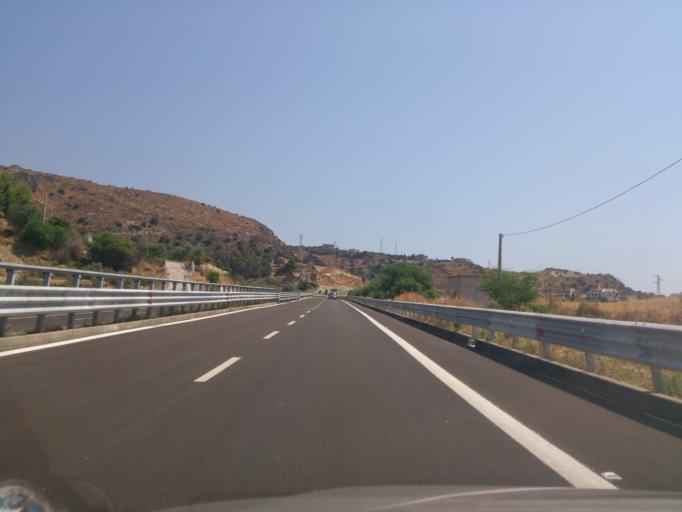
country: IT
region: Calabria
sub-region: Provincia di Reggio Calabria
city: Roccella Ionica
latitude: 38.3270
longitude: 16.3940
